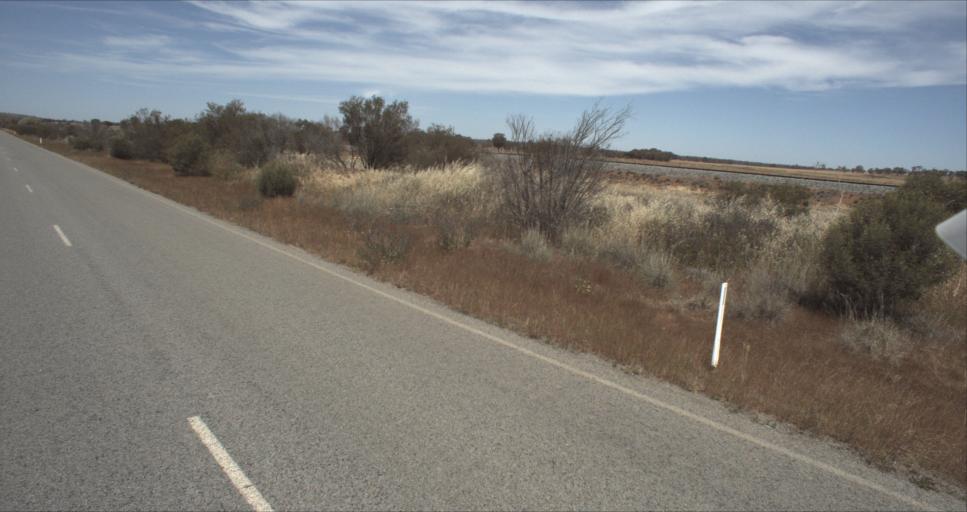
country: AU
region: New South Wales
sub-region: Leeton
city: Leeton
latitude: -34.6252
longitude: 146.4506
